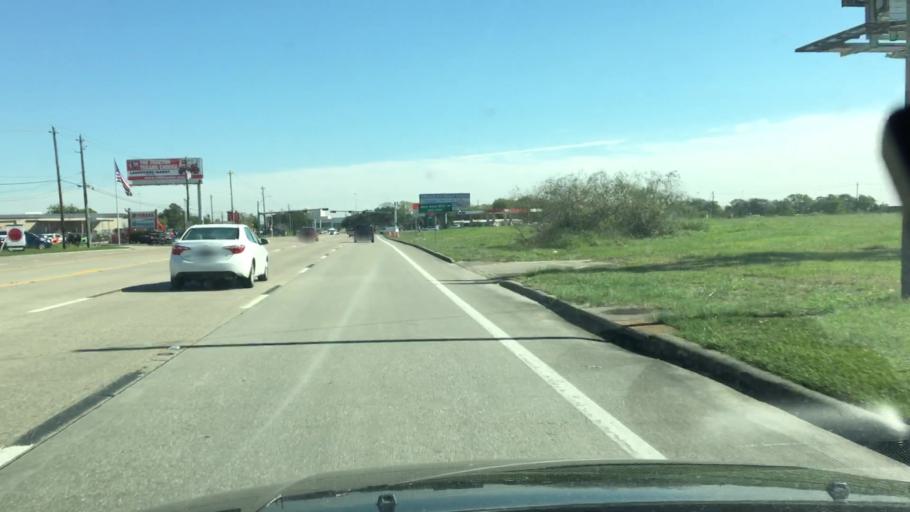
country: US
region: Texas
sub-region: Harris County
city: Webster
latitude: 29.5245
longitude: -95.1406
